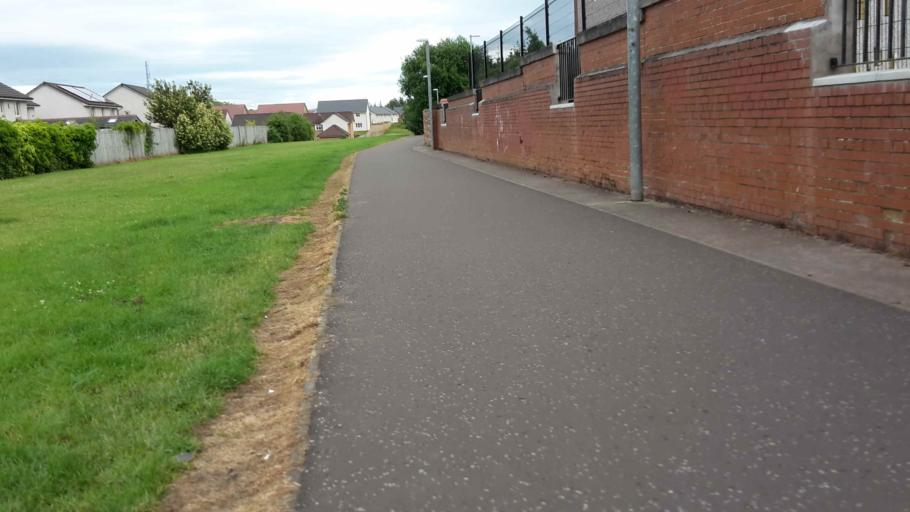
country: GB
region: Scotland
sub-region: South Lanarkshire
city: Uddingston
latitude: 55.8211
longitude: -4.0755
